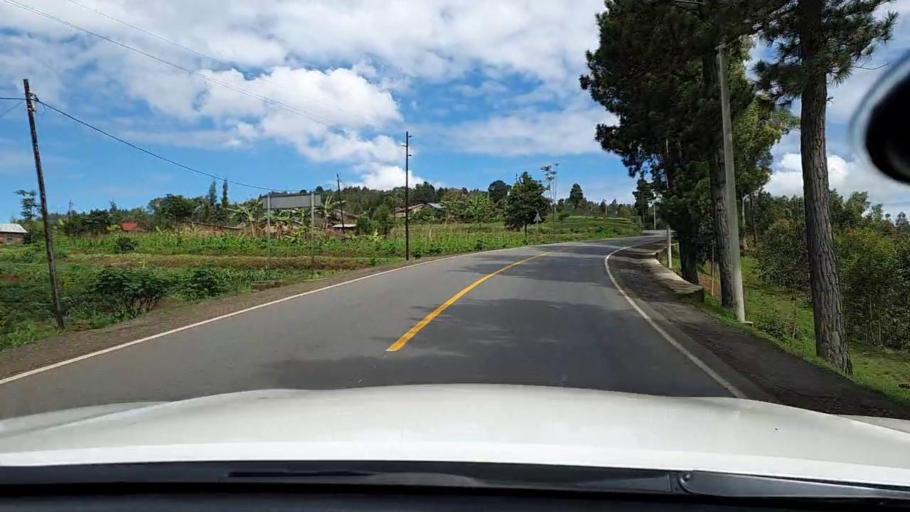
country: RW
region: Kigali
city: Kigali
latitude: -1.8303
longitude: 29.9496
